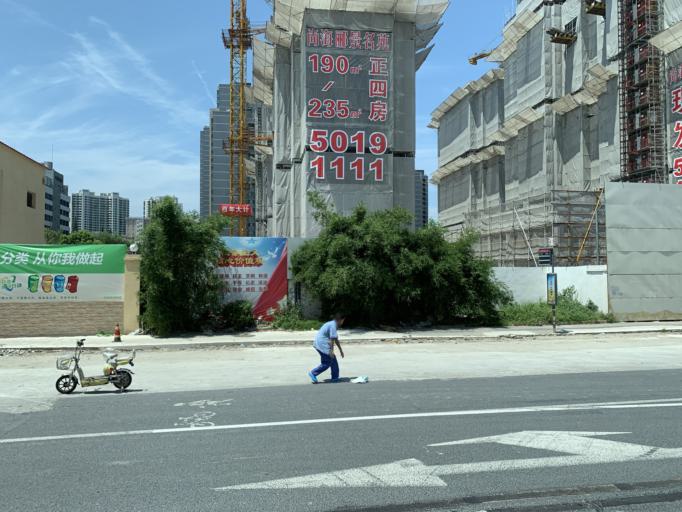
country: CN
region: Shanghai Shi
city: Pudong
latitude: 31.2422
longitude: 121.5378
